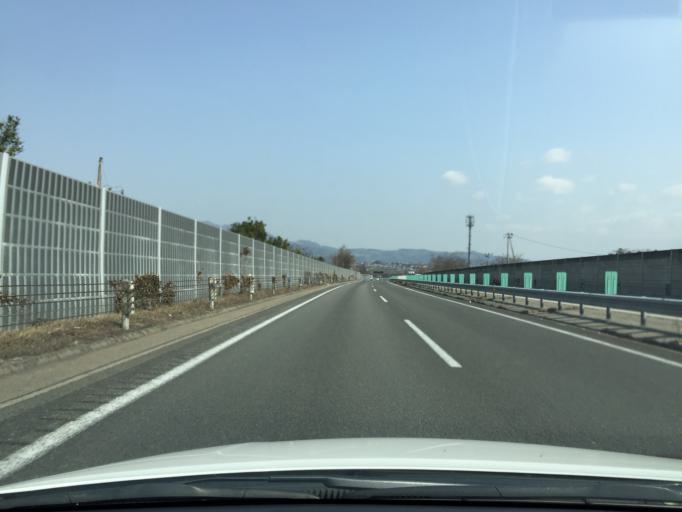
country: JP
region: Miyagi
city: Shiroishi
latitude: 37.9915
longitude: 140.6067
